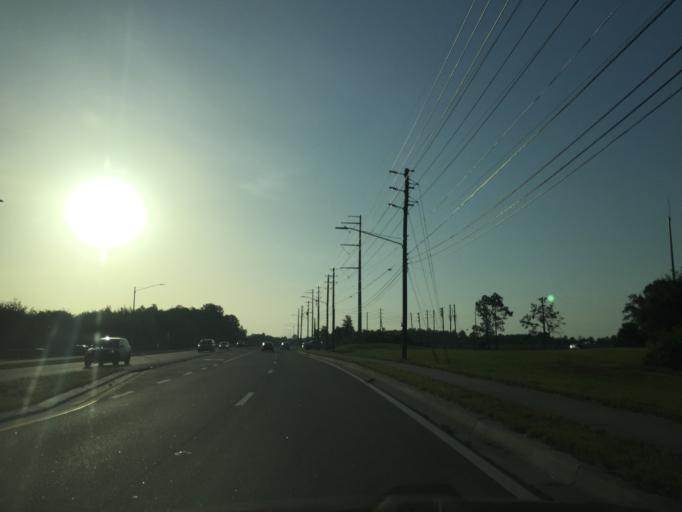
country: US
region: Florida
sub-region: Orange County
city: Alafaya
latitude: 28.5247
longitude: -81.2003
